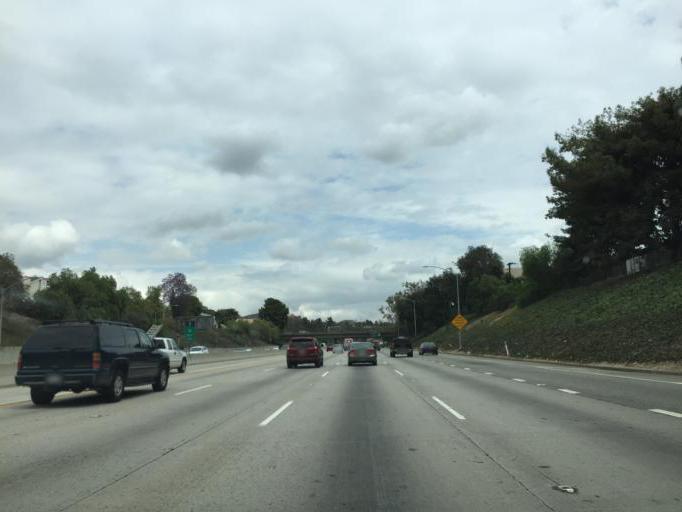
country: US
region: California
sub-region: Los Angeles County
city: Glendale
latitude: 34.1563
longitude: -118.2502
